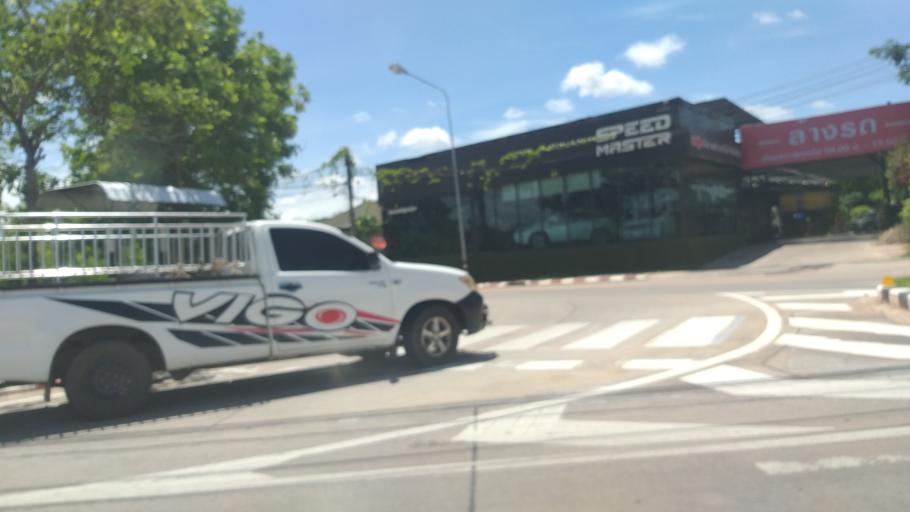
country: TH
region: Khon Kaen
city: Khon Kaen
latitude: 16.4361
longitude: 102.8194
